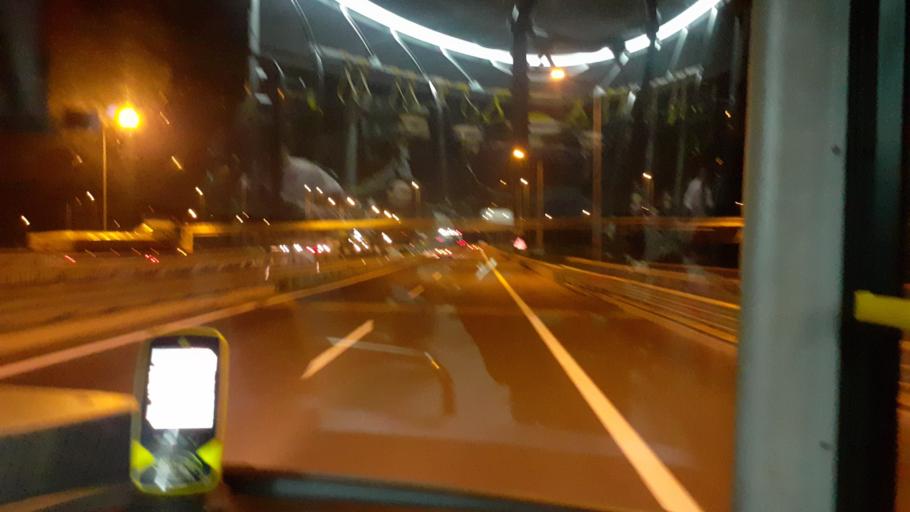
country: TR
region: Istanbul
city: Durusu
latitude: 41.2418
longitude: 28.7653
